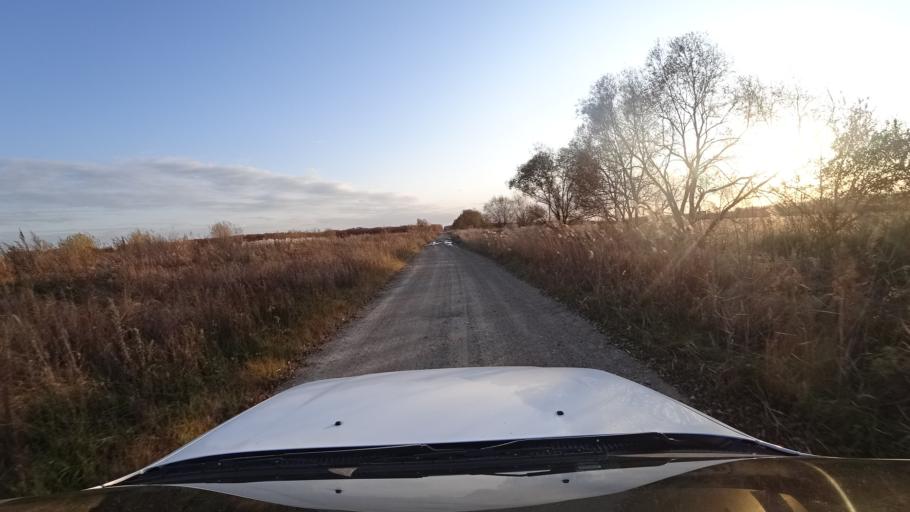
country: RU
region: Primorskiy
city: Lazo
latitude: 45.8117
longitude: 133.6086
